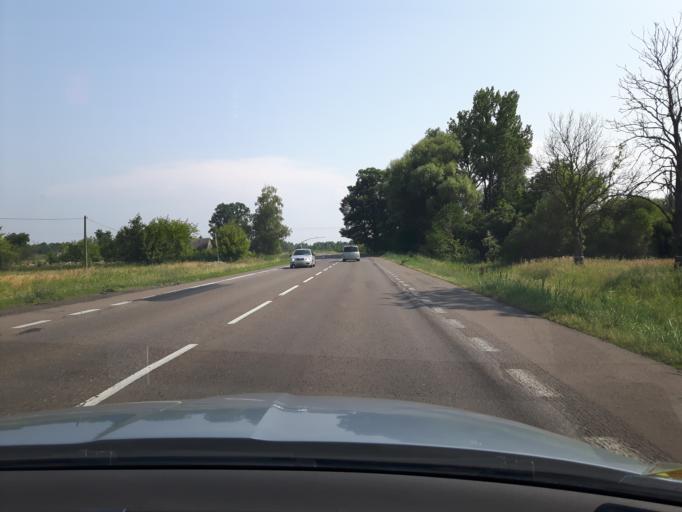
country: PL
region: Masovian Voivodeship
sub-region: Powiat ciechanowski
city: Glinojeck
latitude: 52.7697
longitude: 20.2951
